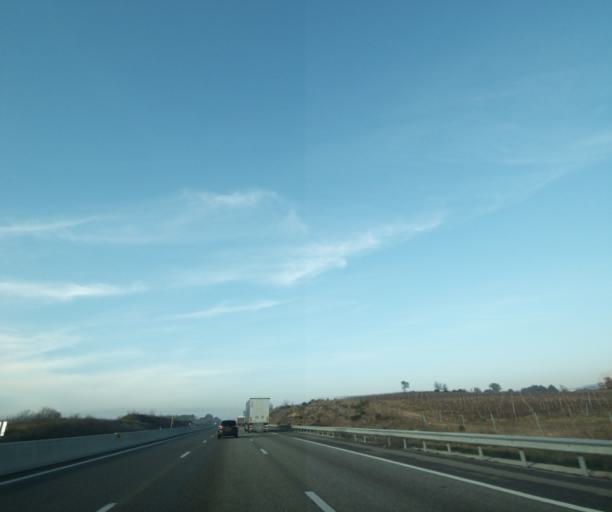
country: FR
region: Provence-Alpes-Cote d'Azur
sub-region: Departement des Bouches-du-Rhone
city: Trets
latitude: 43.4705
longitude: 5.6654
